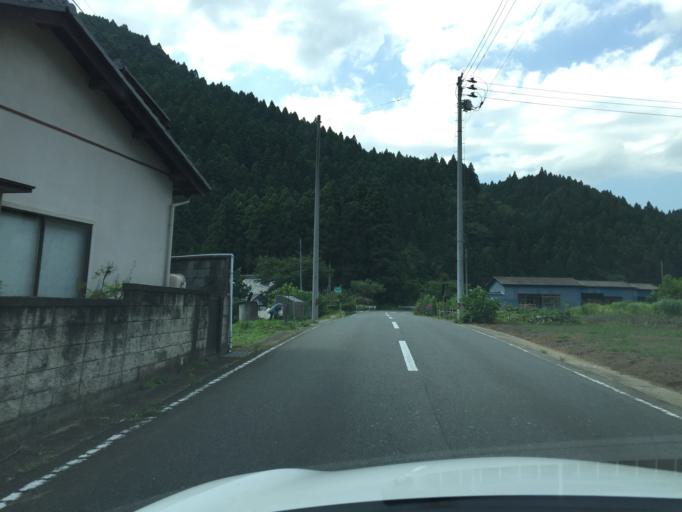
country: JP
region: Fukushima
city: Iwaki
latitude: 37.0248
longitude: 140.7030
